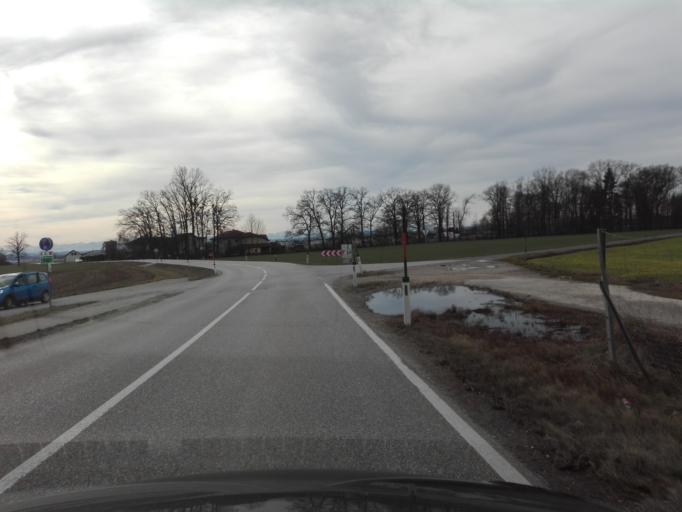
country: AT
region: Upper Austria
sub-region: Politischer Bezirk Perg
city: Perg
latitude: 48.2354
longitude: 14.6230
